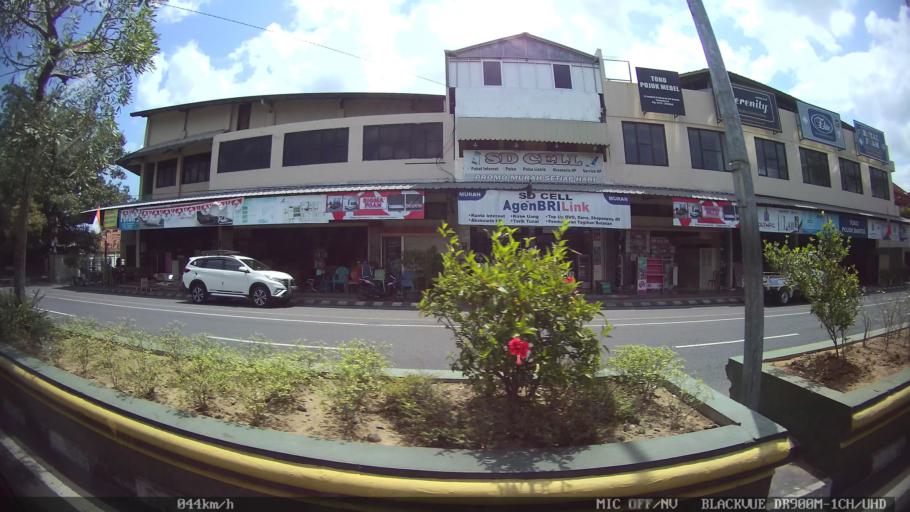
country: ID
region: Daerah Istimewa Yogyakarta
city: Bantul
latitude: -7.8865
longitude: 110.3301
